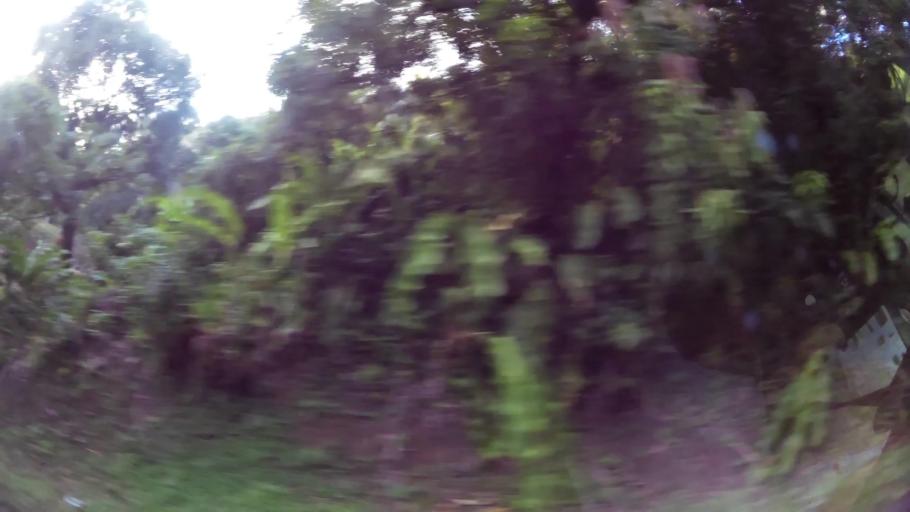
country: DM
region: Saint John
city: Portsmouth
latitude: 15.5750
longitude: -61.4364
